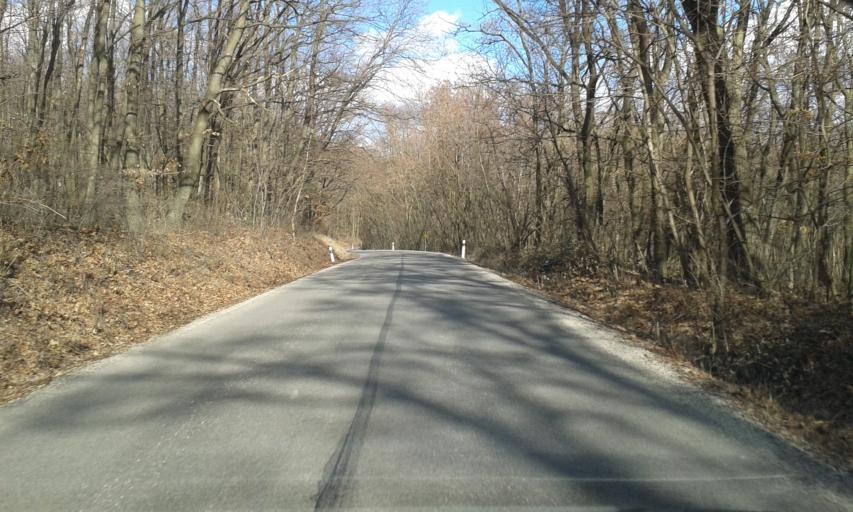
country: SK
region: Nitriansky
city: Zlate Moravce
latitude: 48.4441
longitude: 18.3246
